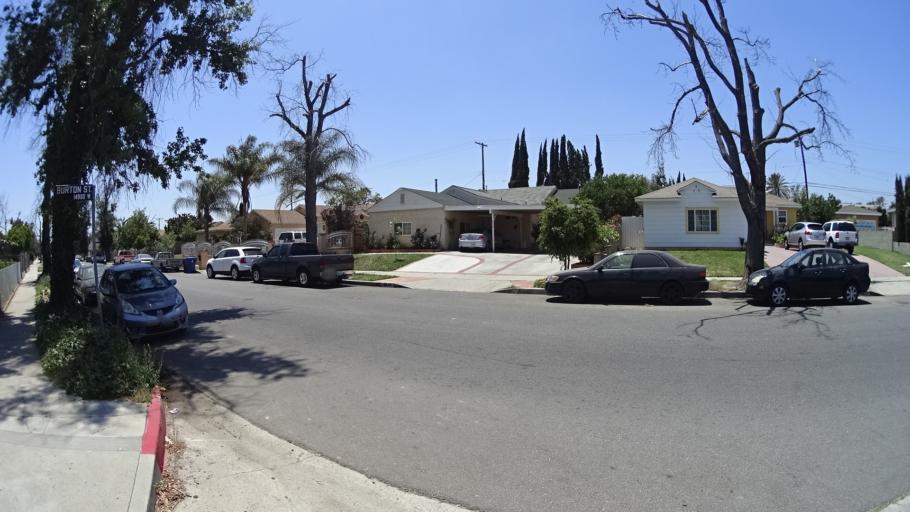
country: US
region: California
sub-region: Los Angeles County
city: Van Nuys
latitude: 34.2205
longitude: -118.4587
